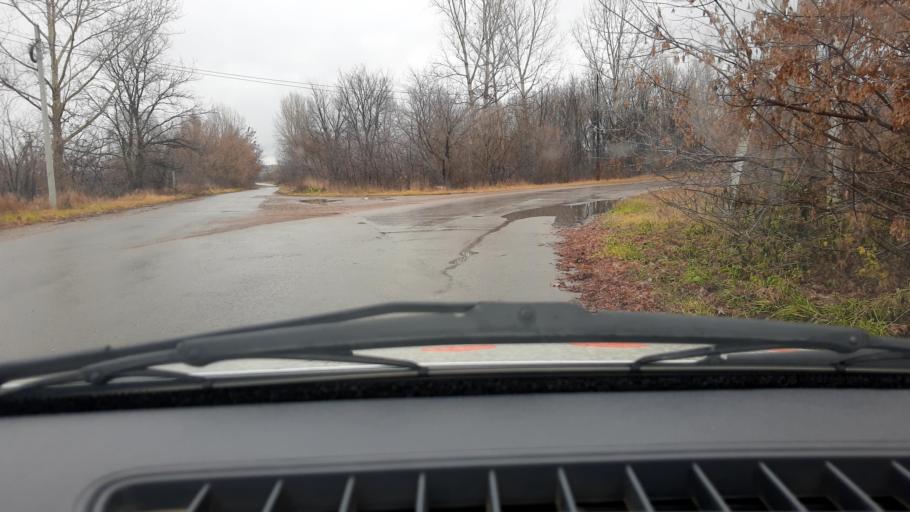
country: RU
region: Bashkortostan
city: Iglino
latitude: 54.7985
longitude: 56.2102
